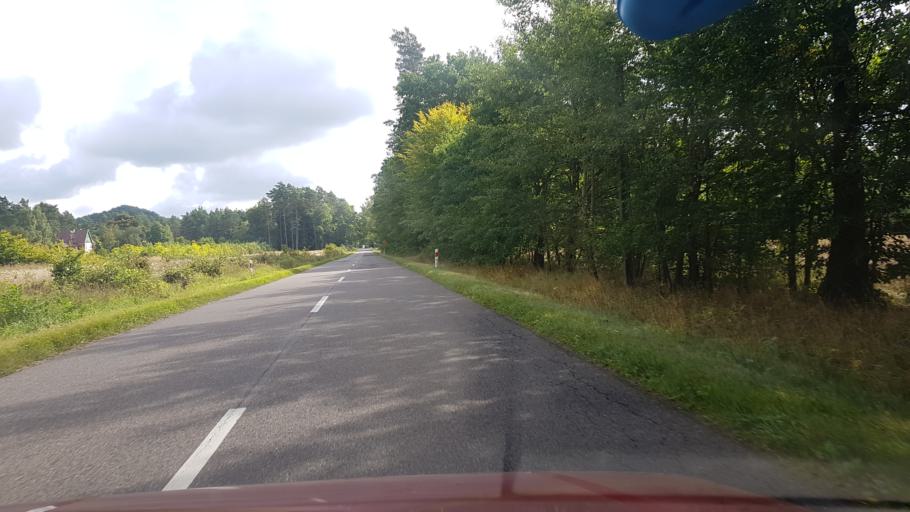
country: PL
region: West Pomeranian Voivodeship
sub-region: Powiat koszalinski
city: Polanow
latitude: 54.1170
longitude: 16.7372
